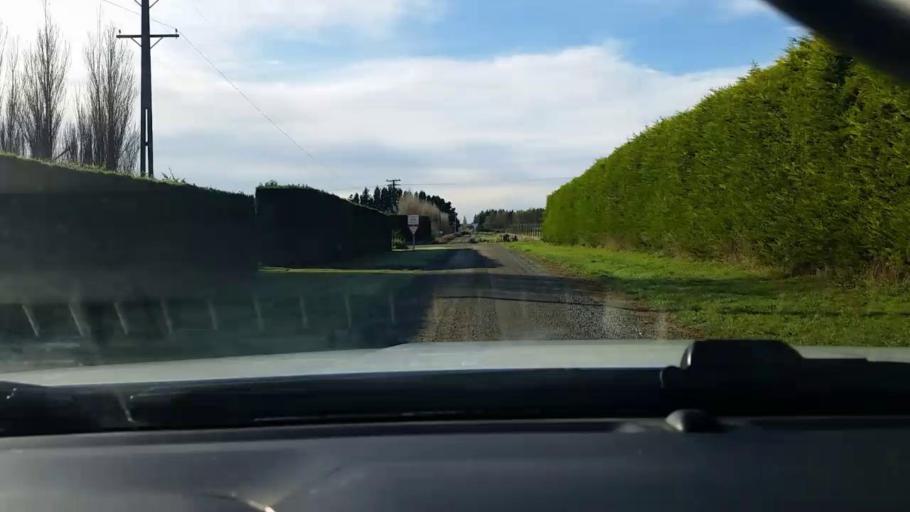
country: NZ
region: Southland
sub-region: Invercargill City
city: Invercargill
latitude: -46.2845
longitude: 168.3449
